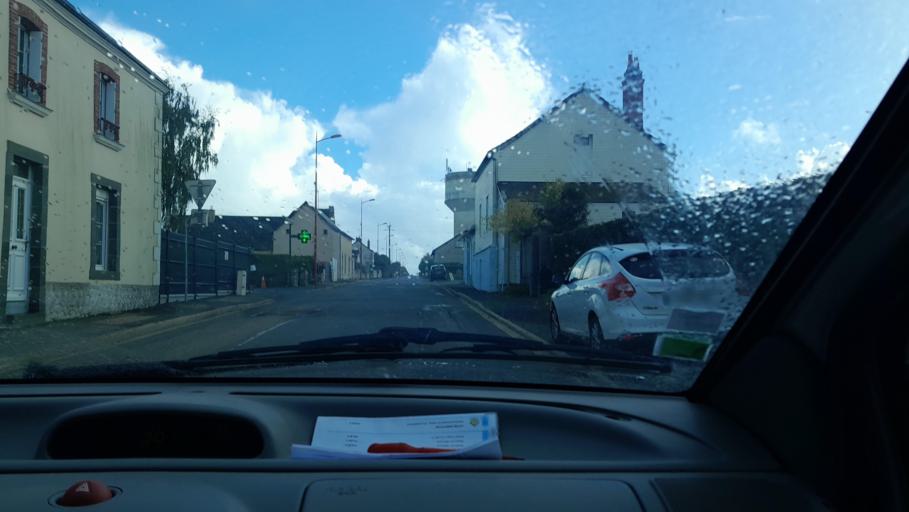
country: FR
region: Pays de la Loire
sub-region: Departement de la Mayenne
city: Cosse-le-Vivien
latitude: 47.9440
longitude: -0.9089
